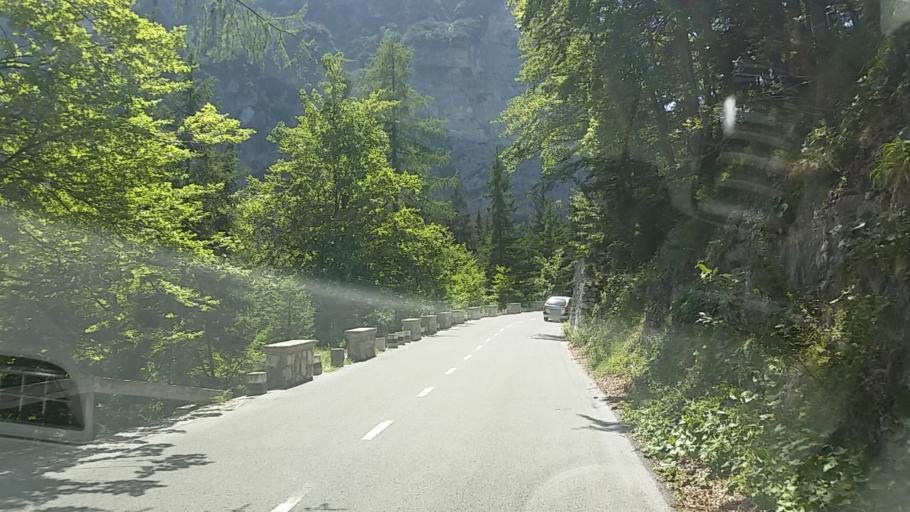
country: SI
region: Kranjska Gora
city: Kranjska Gora
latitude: 46.4446
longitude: 13.7742
